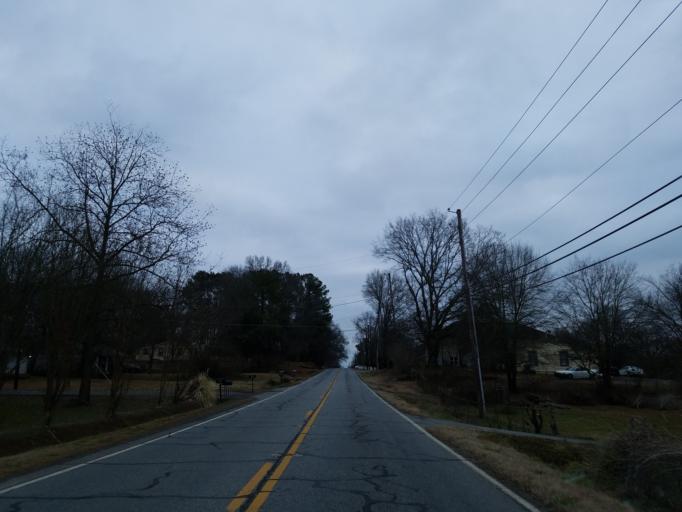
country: US
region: Georgia
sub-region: Bartow County
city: Cartersville
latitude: 34.2092
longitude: -84.8332
